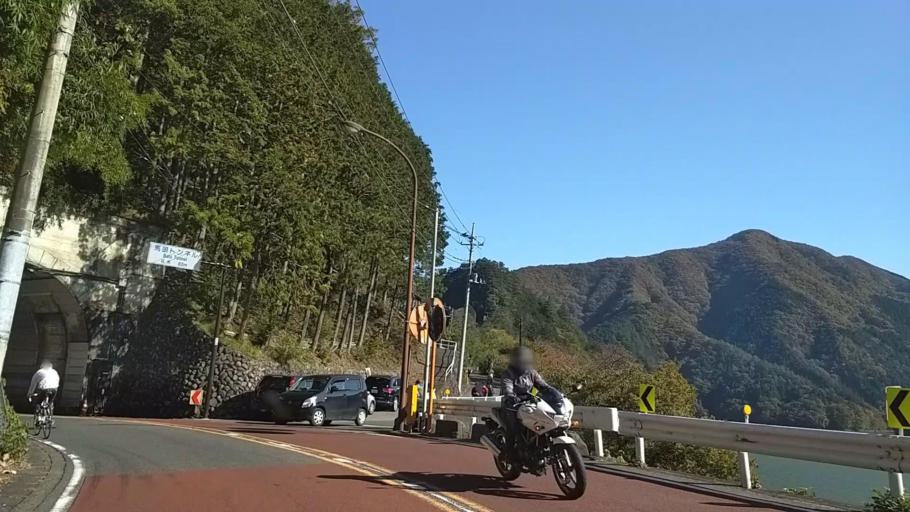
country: JP
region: Yamanashi
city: Uenohara
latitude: 35.7776
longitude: 139.0153
